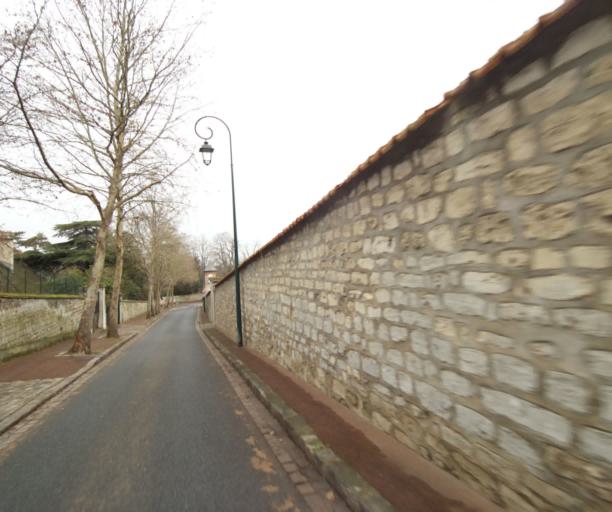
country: FR
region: Ile-de-France
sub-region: Departement des Hauts-de-Seine
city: Rueil-Malmaison
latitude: 48.8697
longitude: 2.1699
